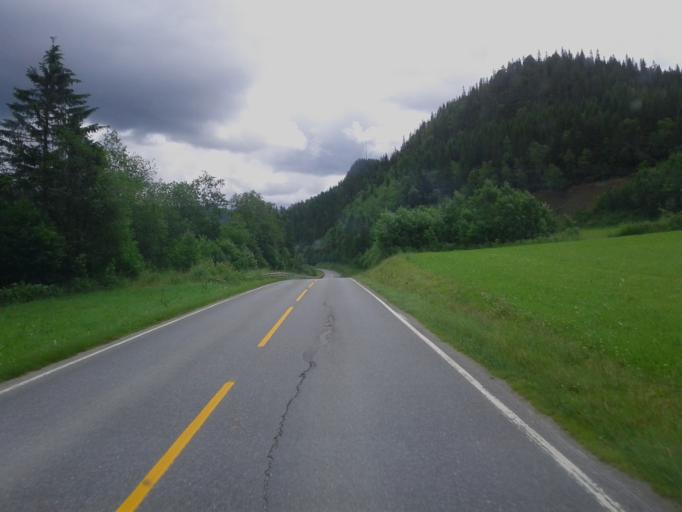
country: NO
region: Sor-Trondelag
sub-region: Midtre Gauldal
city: Storen
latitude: 62.9443
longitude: 10.6325
